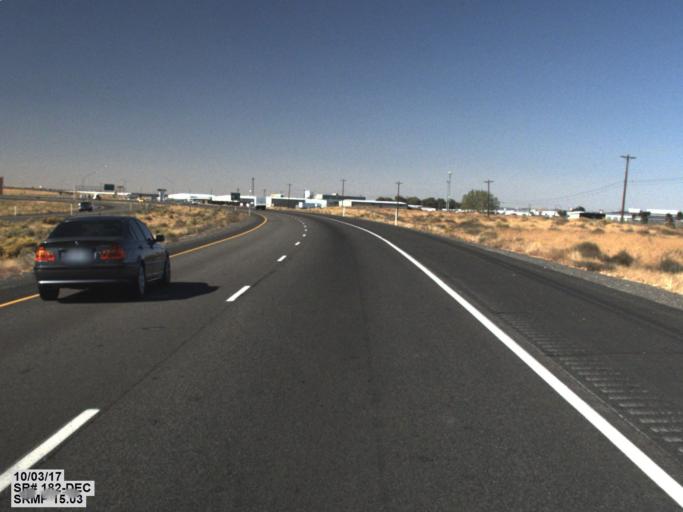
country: US
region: Washington
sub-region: Franklin County
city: Pasco
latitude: 46.2487
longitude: -119.0699
